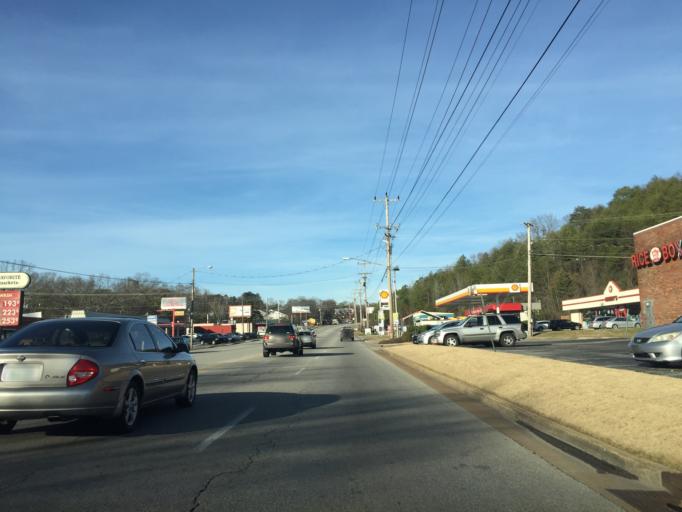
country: US
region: Tennessee
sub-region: Hamilton County
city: Red Bank
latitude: 35.1072
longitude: -85.2720
